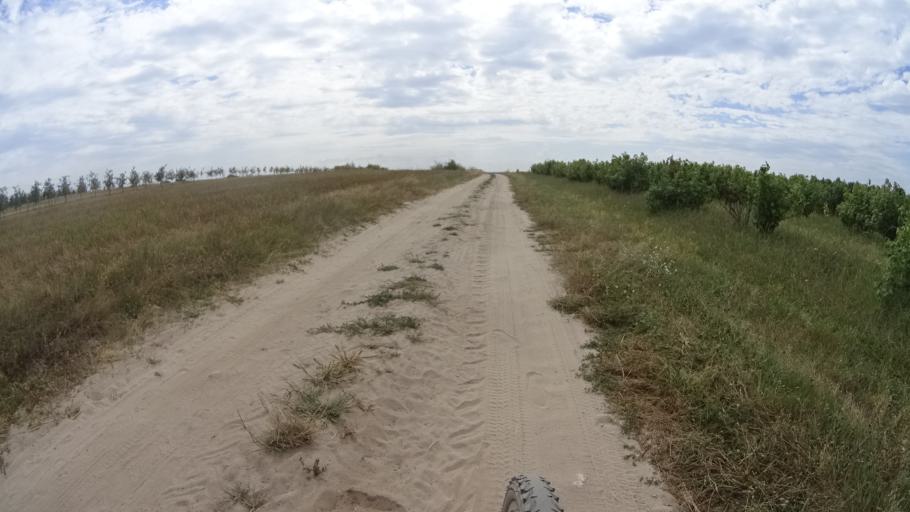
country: PL
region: Masovian Voivodeship
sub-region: Powiat bialobrzeski
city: Wysmierzyce
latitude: 51.6561
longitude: 20.7956
